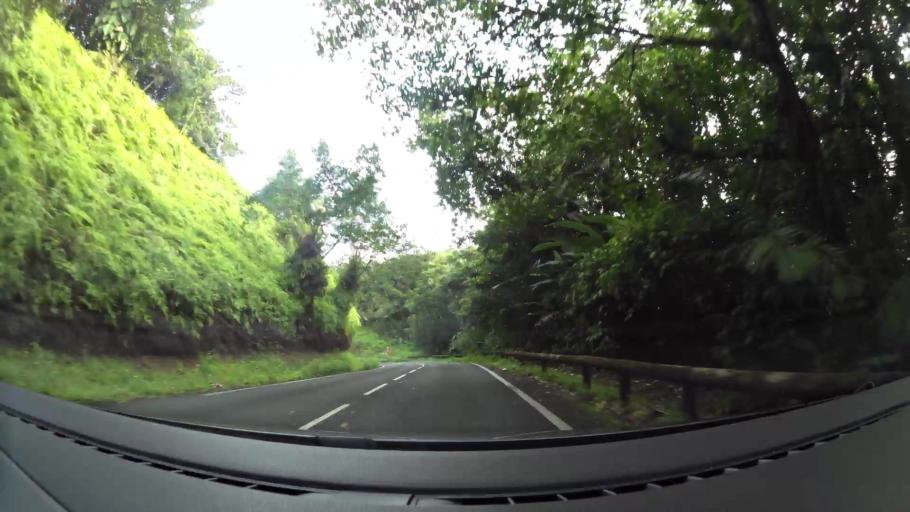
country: GP
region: Guadeloupe
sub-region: Guadeloupe
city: Bouillante
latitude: 16.1781
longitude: -61.7193
